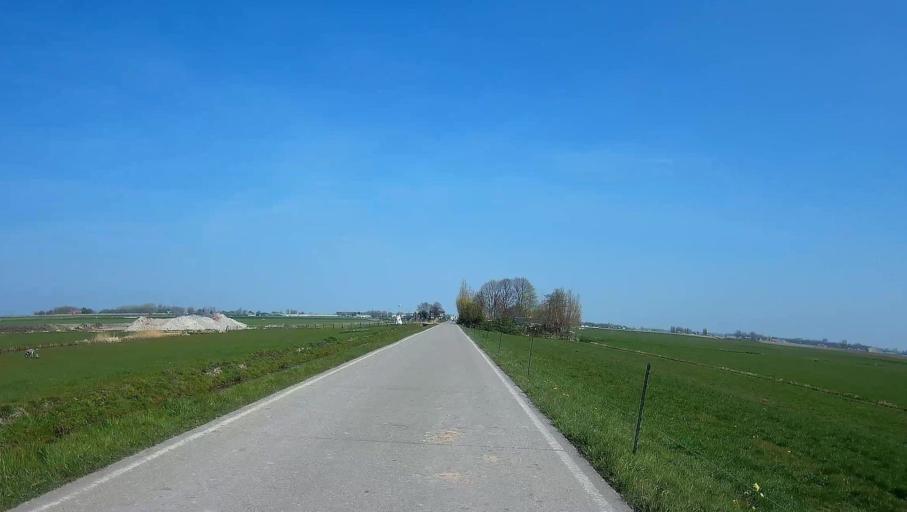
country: NL
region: South Holland
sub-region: Gemeente Schiedam
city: Schiedam
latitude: 51.9649
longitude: 4.4159
